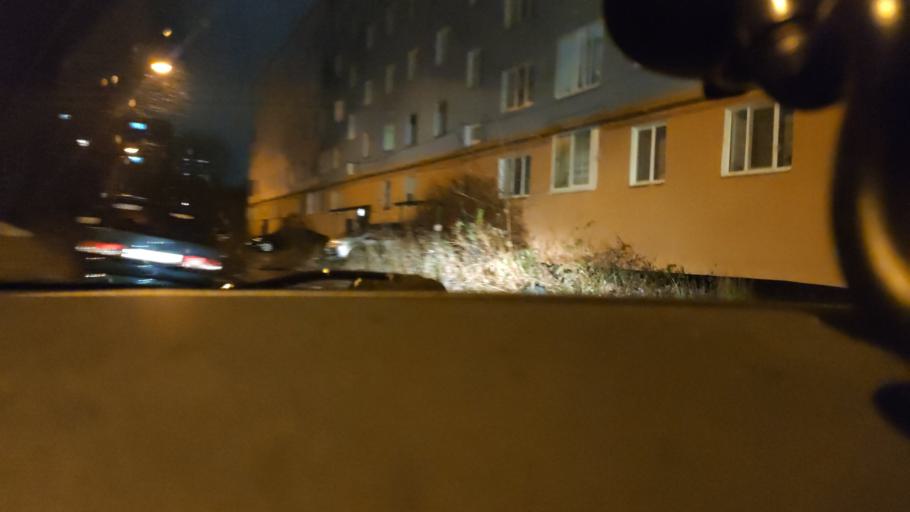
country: RU
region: Perm
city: Perm
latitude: 57.9615
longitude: 56.2144
